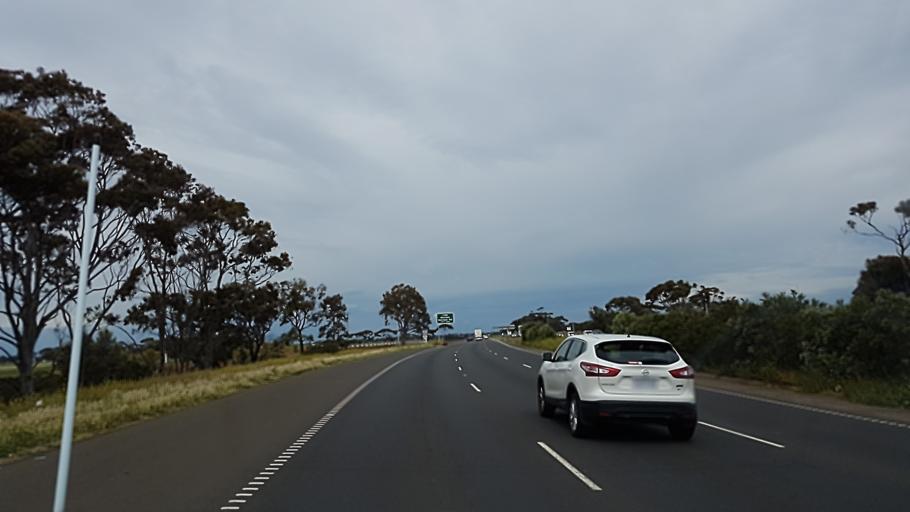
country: AU
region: Victoria
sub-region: Wyndham
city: Hoppers Crossing
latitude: -37.8989
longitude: 144.7065
